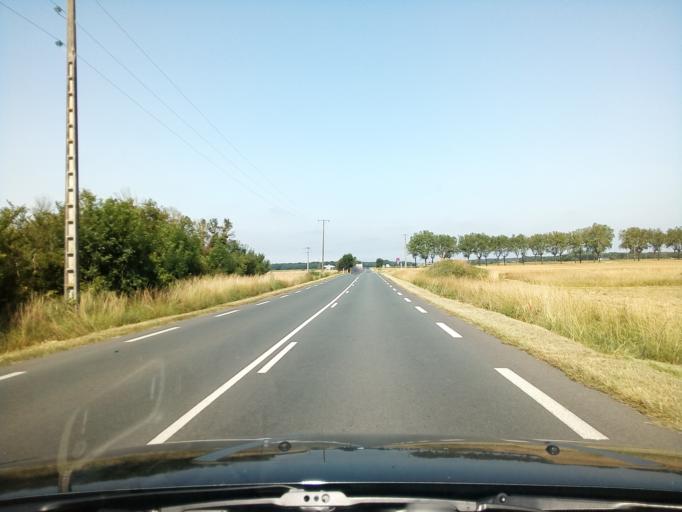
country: FR
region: Poitou-Charentes
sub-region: Departement de la Charente-Maritime
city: Le Gua
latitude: 45.7629
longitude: -0.9775
